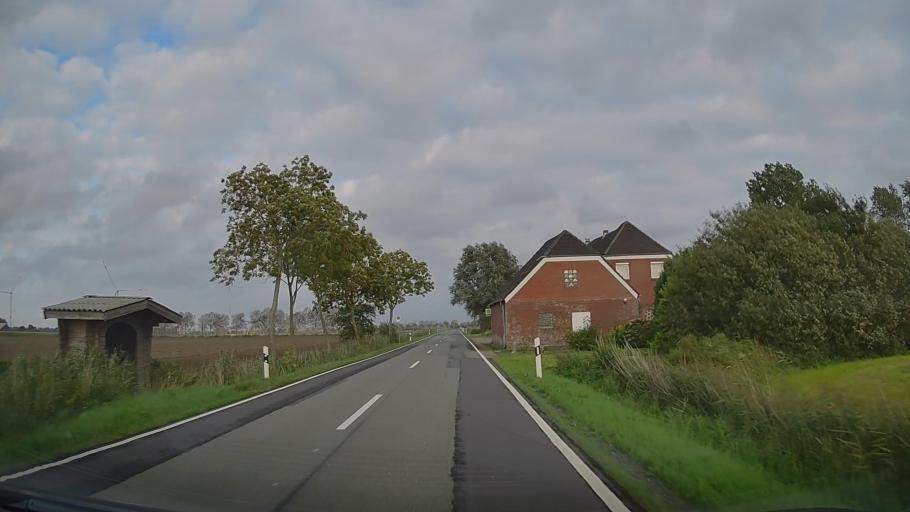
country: DE
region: Schleswig-Holstein
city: Simonsberg
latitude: 54.4392
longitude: 9.0272
